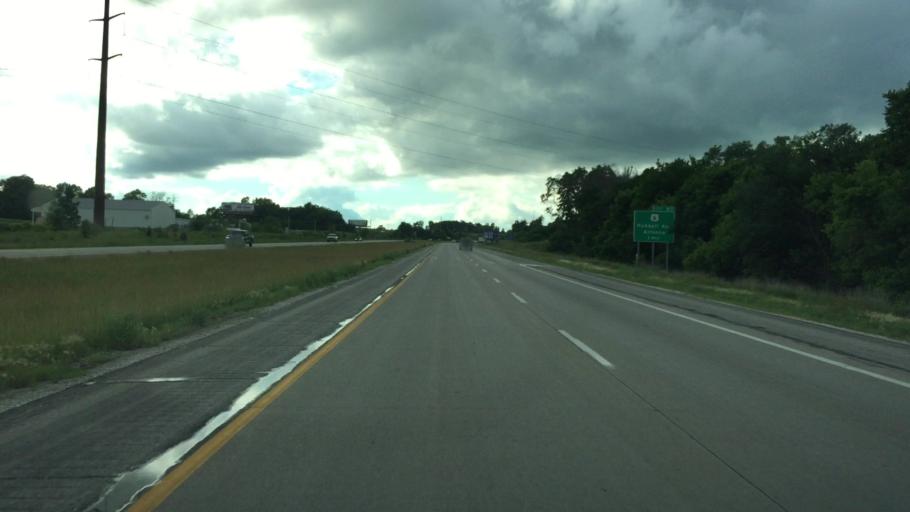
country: US
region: Iowa
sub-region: Polk County
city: Altoona
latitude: 41.6259
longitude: -93.4966
